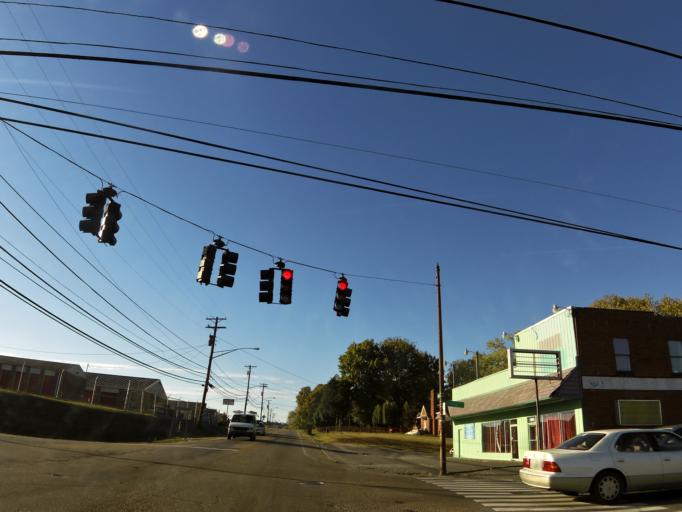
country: US
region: Tennessee
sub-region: Knox County
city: Knoxville
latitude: 36.0082
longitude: -83.9665
